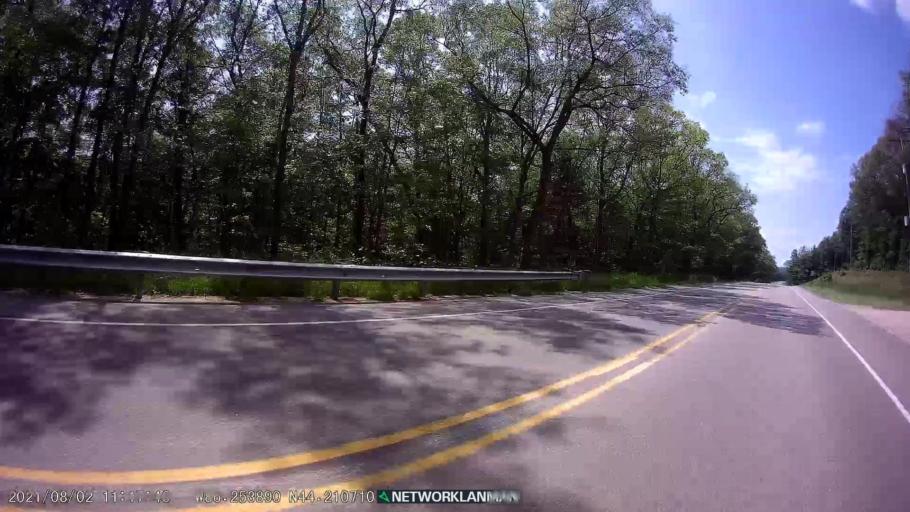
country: US
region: Michigan
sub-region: Manistee County
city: Manistee
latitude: 44.2107
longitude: -86.2541
